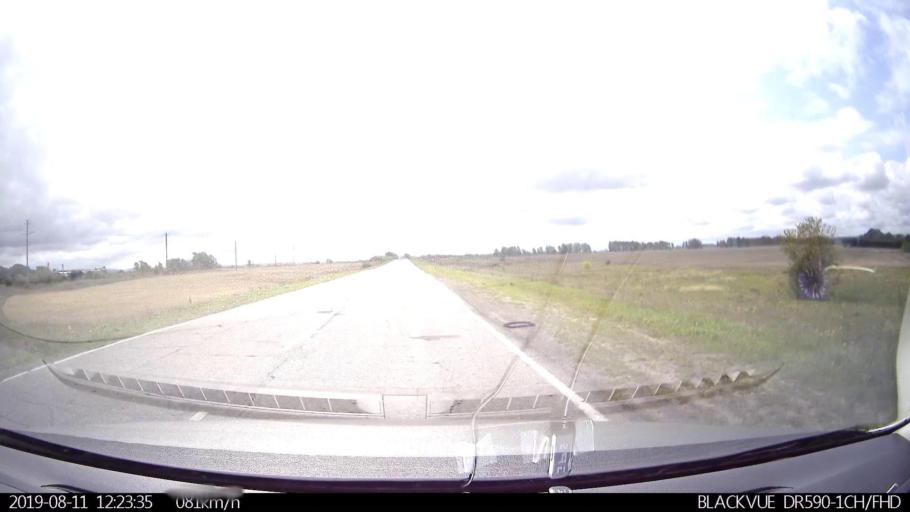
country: RU
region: Ulyanovsk
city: Ignatovka
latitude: 53.8937
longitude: 47.9503
